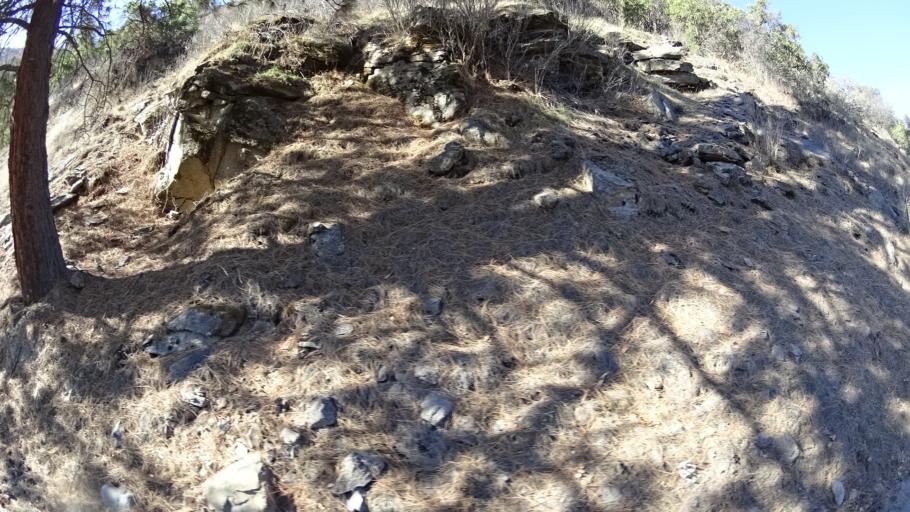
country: US
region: California
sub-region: Siskiyou County
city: Yreka
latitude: 41.8442
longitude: -122.6846
